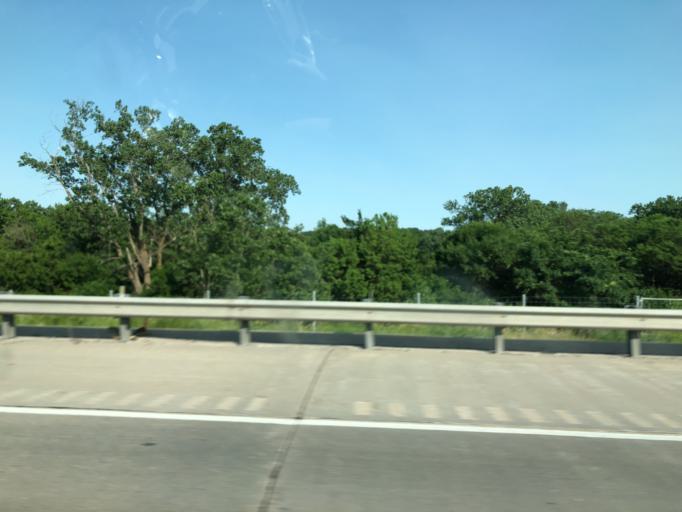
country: US
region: Nebraska
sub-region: Saunders County
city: Ashland
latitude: 41.0235
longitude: -96.2999
